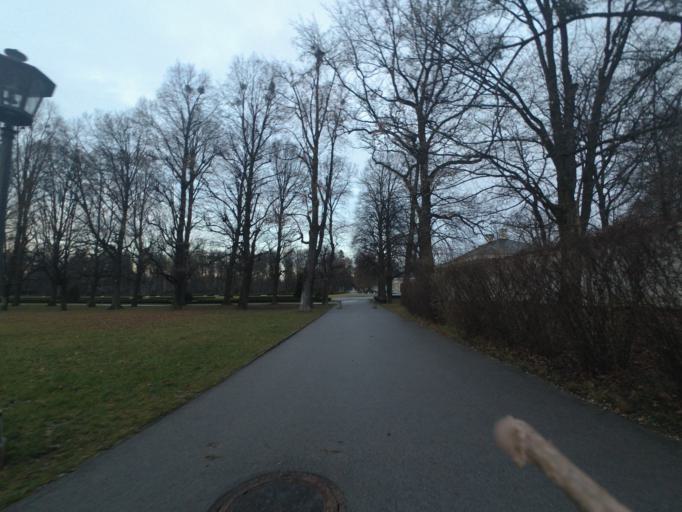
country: DE
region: Bavaria
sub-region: Upper Bavaria
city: Freilassing
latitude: 47.8177
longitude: 12.9948
